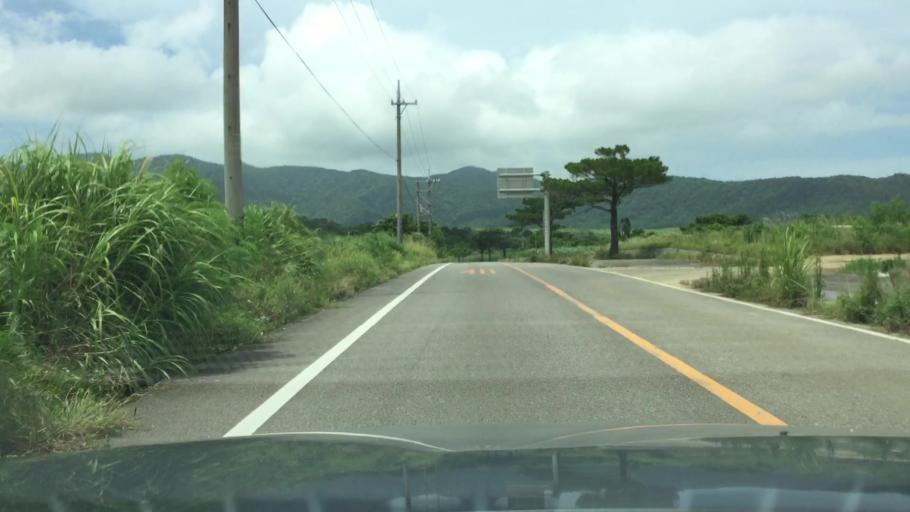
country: JP
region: Okinawa
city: Ishigaki
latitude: 24.4126
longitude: 124.2145
